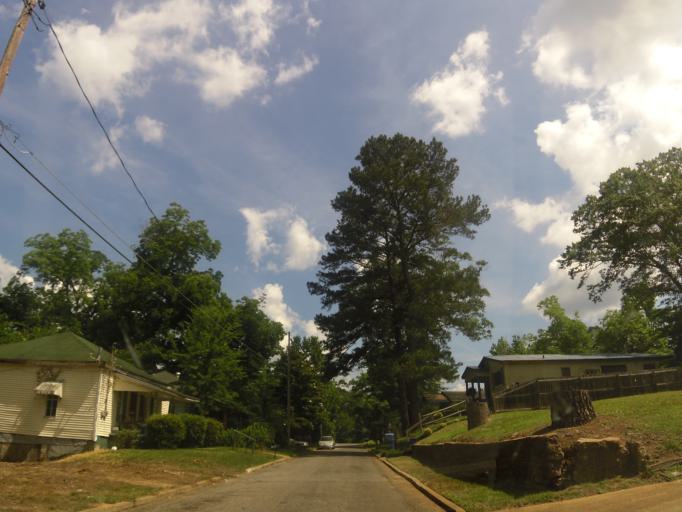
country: US
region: Mississippi
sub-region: Lauderdale County
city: Meridian
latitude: 32.3794
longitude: -88.7096
